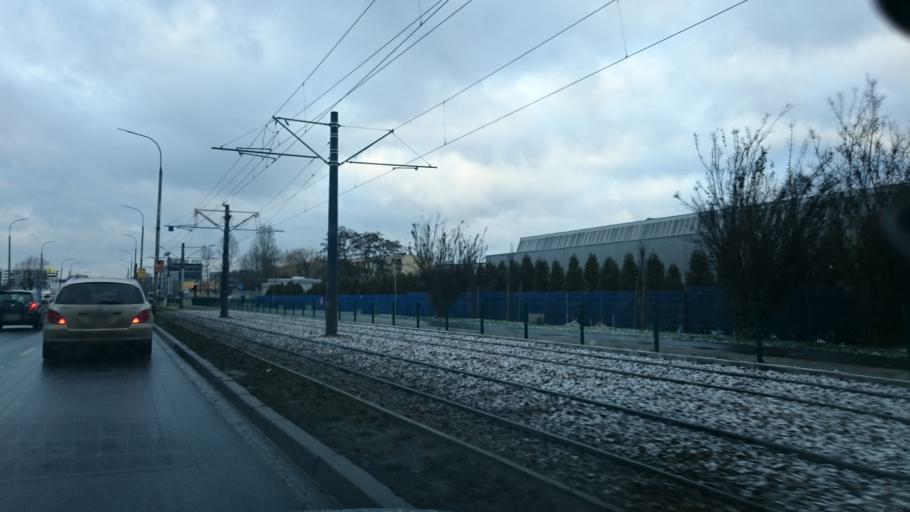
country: PL
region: Lesser Poland Voivodeship
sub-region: Krakow
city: Krakow
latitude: 50.0299
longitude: 19.9738
